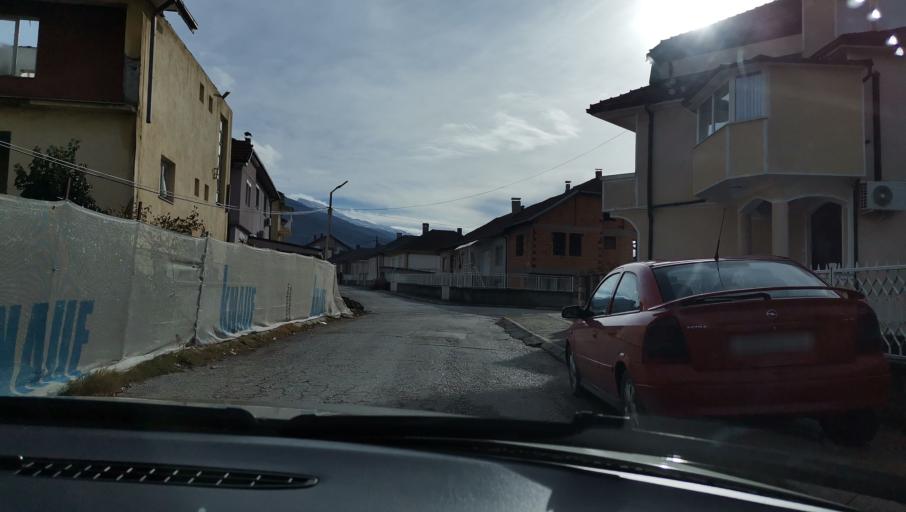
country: MK
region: Debar
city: Debar
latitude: 41.5168
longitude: 20.5306
